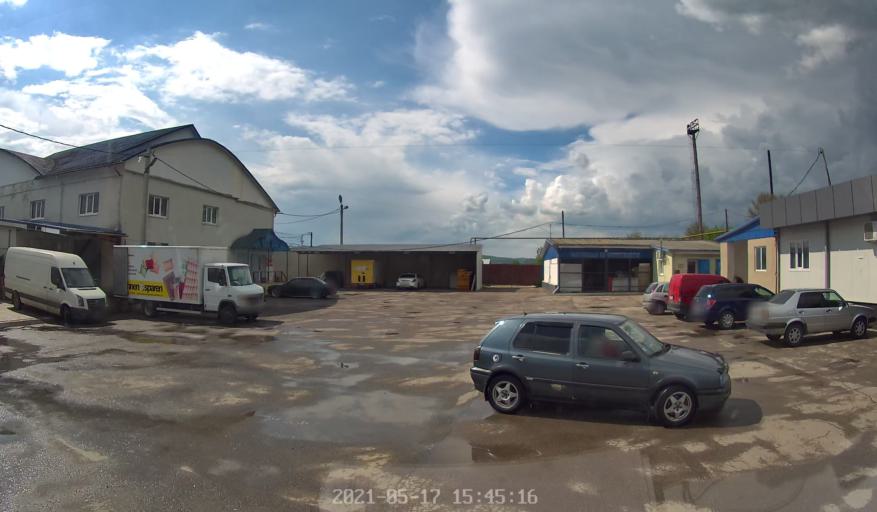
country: MD
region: Hincesti
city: Hincesti
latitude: 46.8340
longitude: 28.5990
